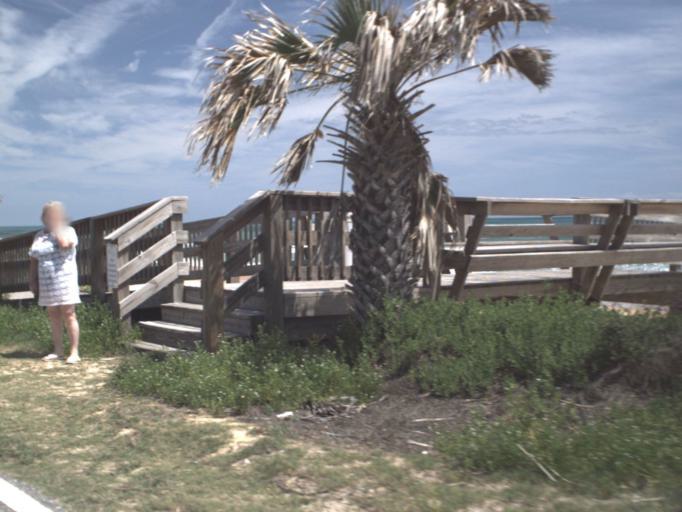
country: US
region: Florida
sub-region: Flagler County
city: Flagler Beach
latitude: 29.4294
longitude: -81.1036
